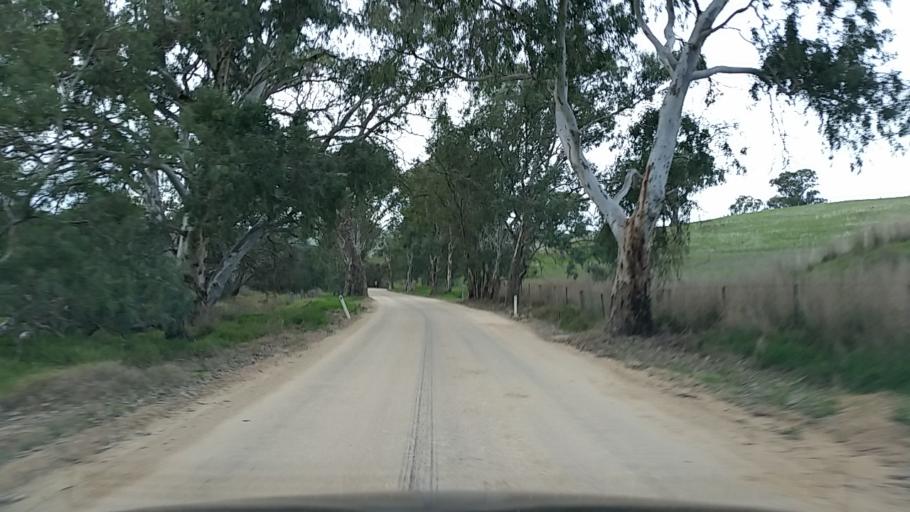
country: AU
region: South Australia
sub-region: Mount Barker
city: Nairne
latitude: -34.9555
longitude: 139.0115
